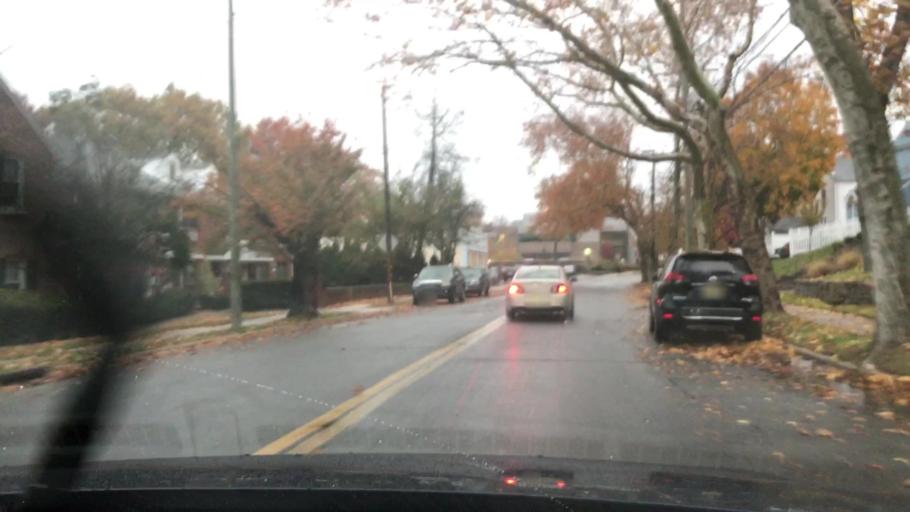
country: US
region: New Jersey
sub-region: Bergen County
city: Bogota
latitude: 40.8851
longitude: -74.0214
